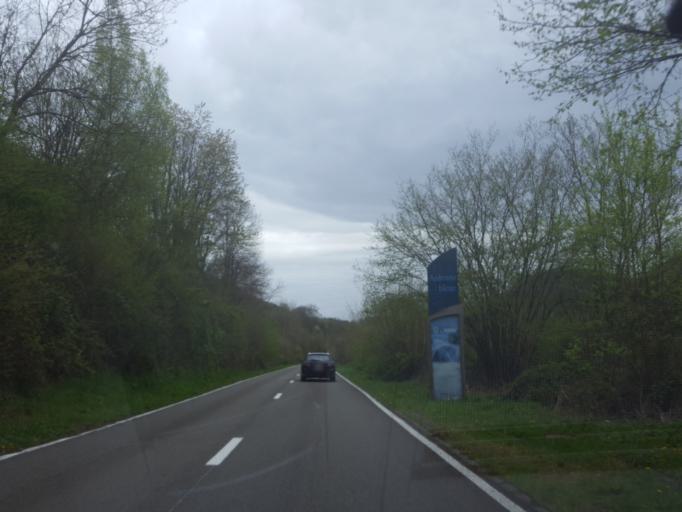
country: BE
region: Wallonia
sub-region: Province de Liege
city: Aywaille
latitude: 50.4467
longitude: 5.7388
